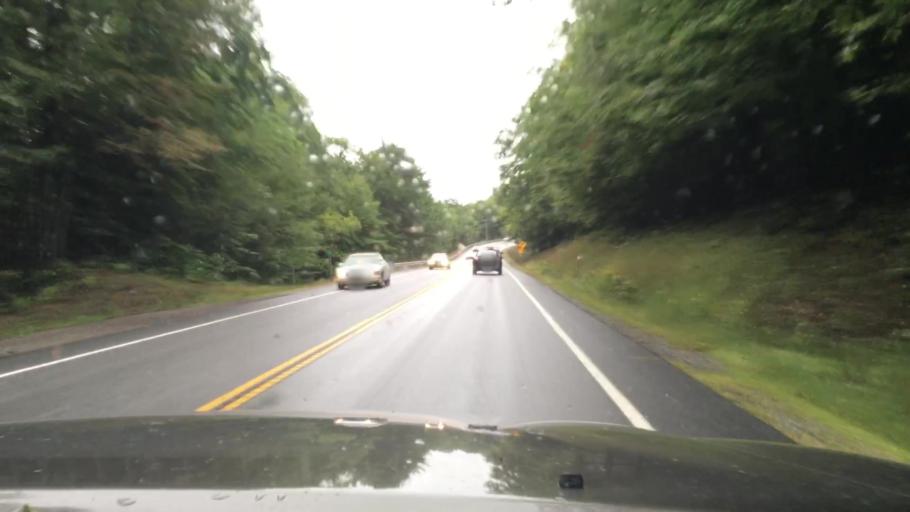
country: US
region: New Hampshire
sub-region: Hillsborough County
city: Antrim
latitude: 43.0689
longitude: -72.0535
